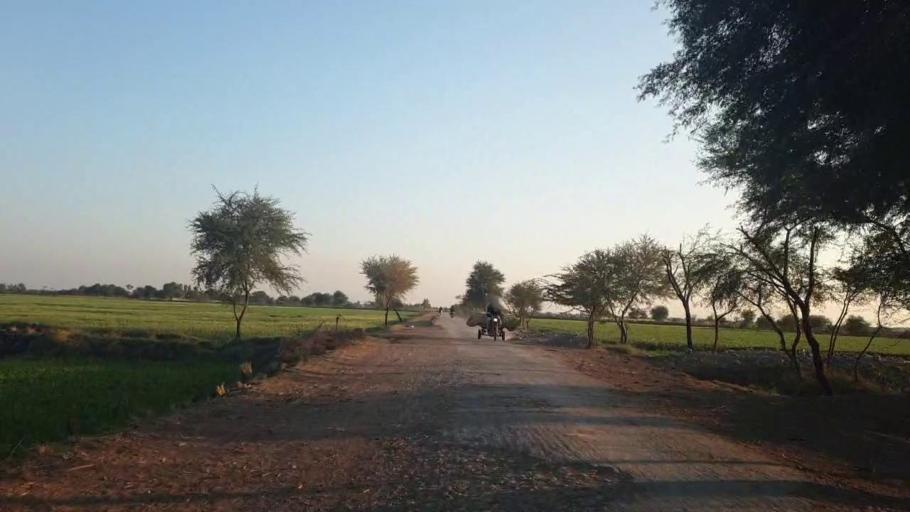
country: PK
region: Sindh
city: Khadro
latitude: 26.0812
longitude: 68.6985
